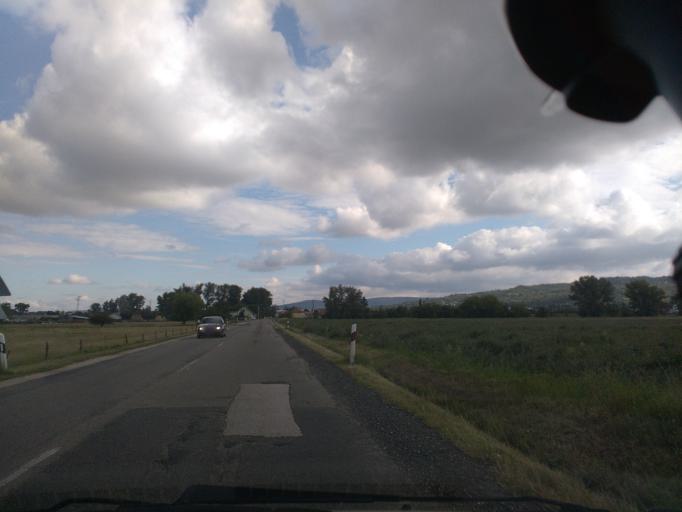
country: HU
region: Komarom-Esztergom
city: Esztergom
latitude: 47.7649
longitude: 18.7371
